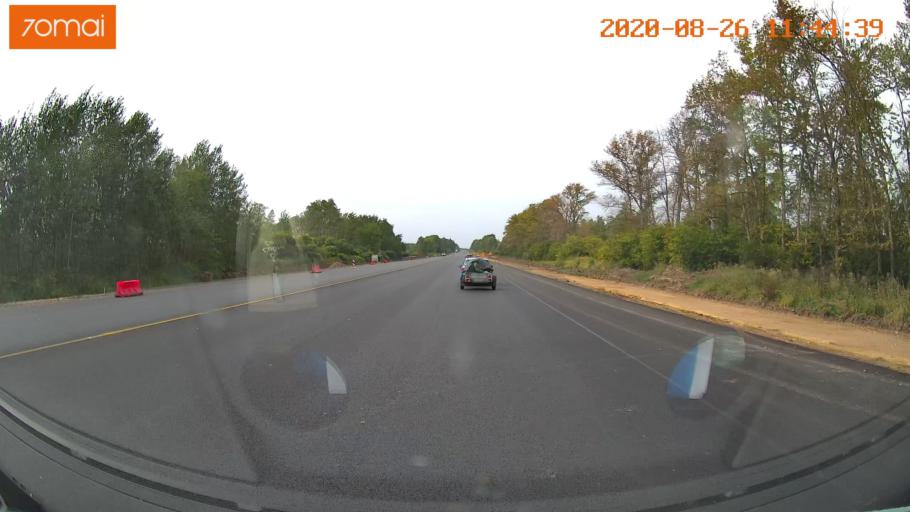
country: RU
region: Rjazan
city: Lesnoy
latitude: 54.2987
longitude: 40.6484
